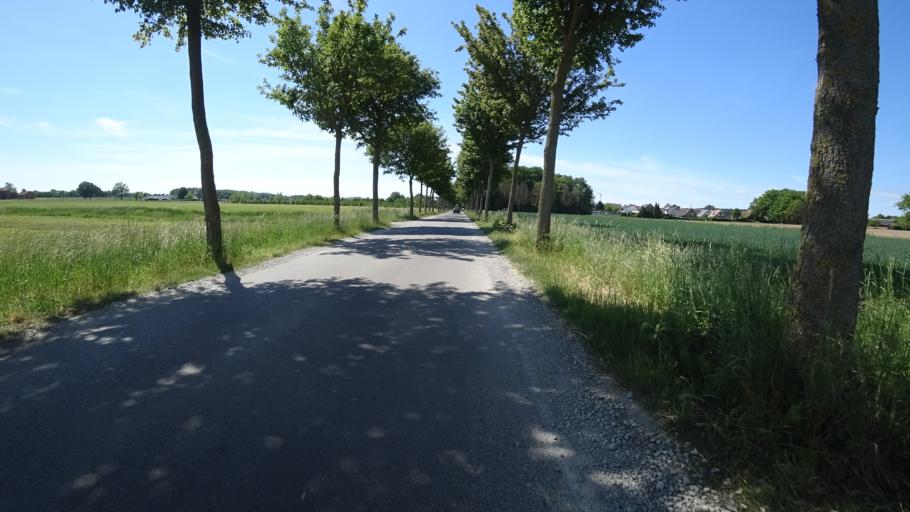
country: DE
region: North Rhine-Westphalia
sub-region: Regierungsbezirk Detmold
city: Rheda-Wiedenbruck
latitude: 51.8208
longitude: 8.2838
